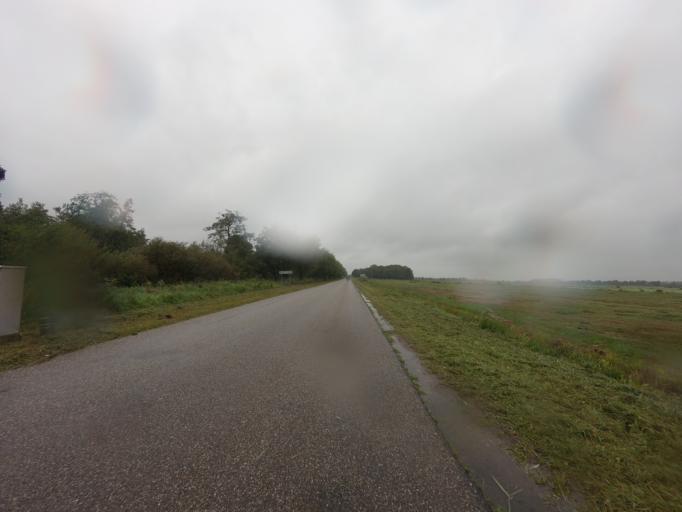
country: NL
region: Friesland
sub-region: Gemeente Tytsjerksteradiel
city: Garyp
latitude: 53.1328
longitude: 5.9571
